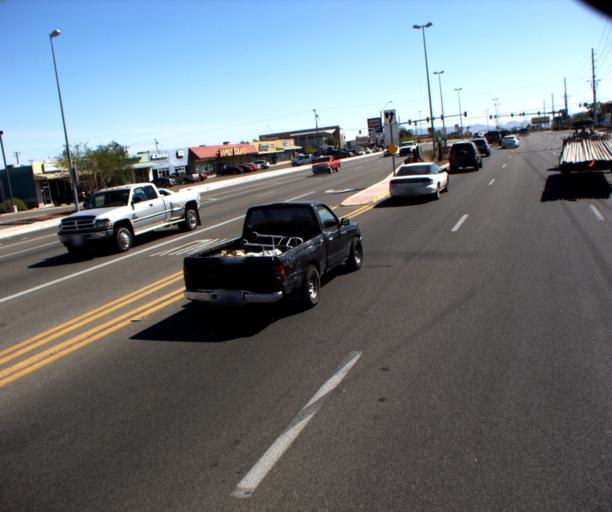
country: US
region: Arizona
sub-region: Yuma County
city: Yuma
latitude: 32.6985
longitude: -114.6180
